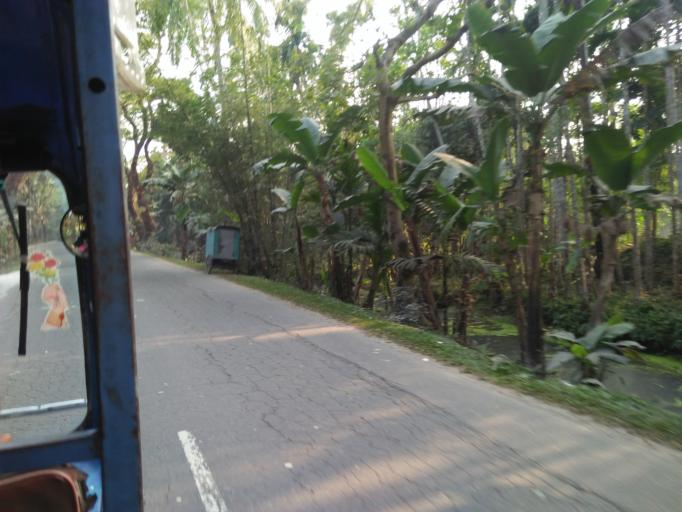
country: BD
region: Barisal
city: Bhola
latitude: 22.7047
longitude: 90.6405
